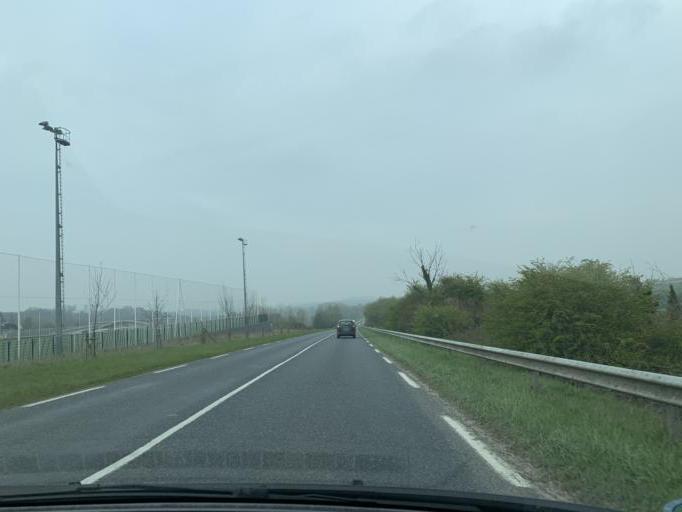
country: FR
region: Nord-Pas-de-Calais
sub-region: Departement du Pas-de-Calais
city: Montreuil
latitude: 50.4525
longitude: 1.7586
